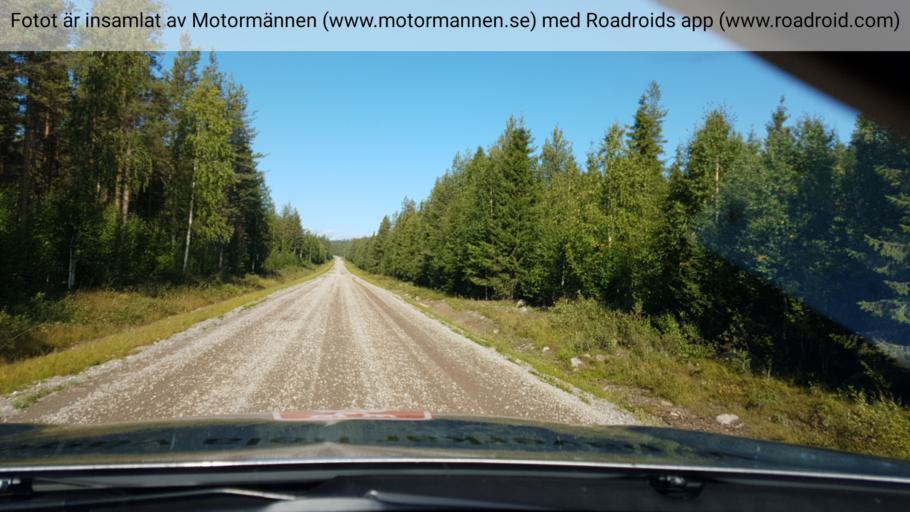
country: SE
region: Norrbotten
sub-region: Overkalix Kommun
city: OEverkalix
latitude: 66.2396
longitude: 23.1518
